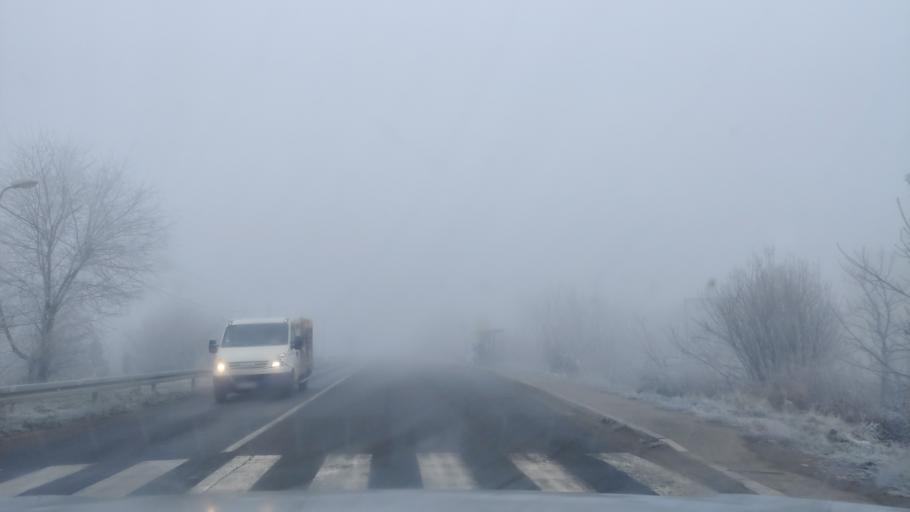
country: RS
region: Central Serbia
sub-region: Belgrade
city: Stari Grad
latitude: 44.8918
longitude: 20.4579
